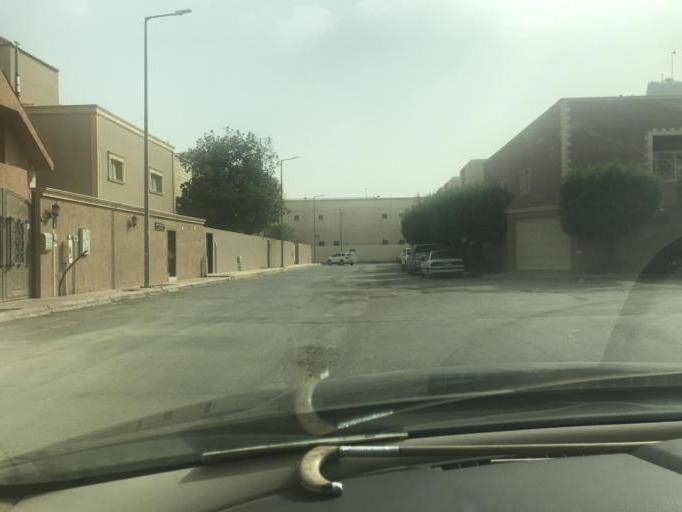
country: SA
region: Ar Riyad
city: Riyadh
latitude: 24.7327
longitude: 46.7877
